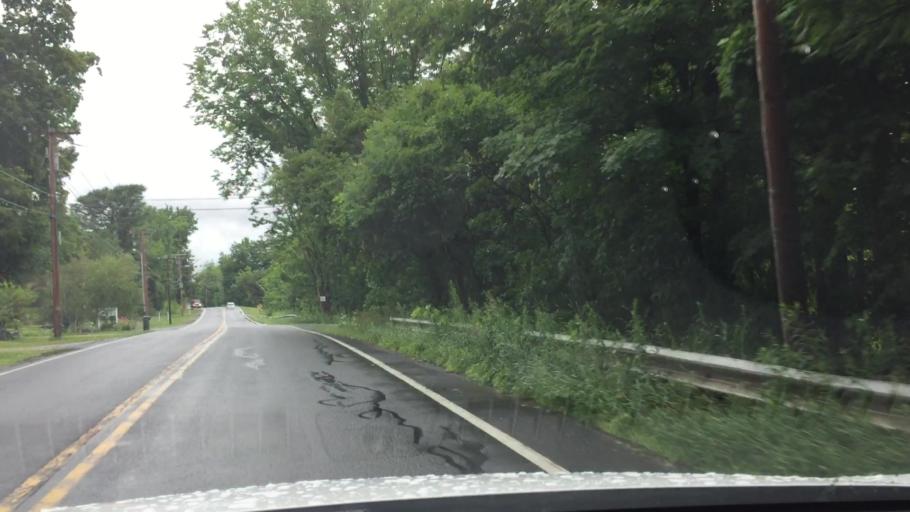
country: US
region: Massachusetts
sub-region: Berkshire County
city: Lenox
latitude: 42.4153
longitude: -73.3120
